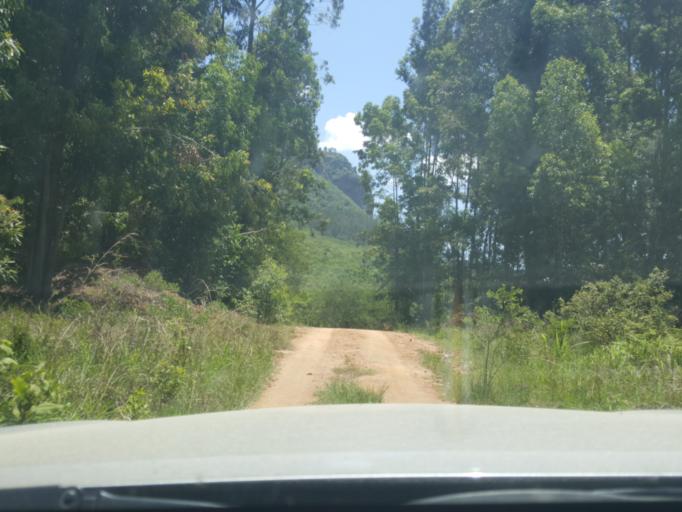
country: ZA
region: Limpopo
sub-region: Mopani District Municipality
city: Hoedspruit
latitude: -24.5970
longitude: 30.8536
